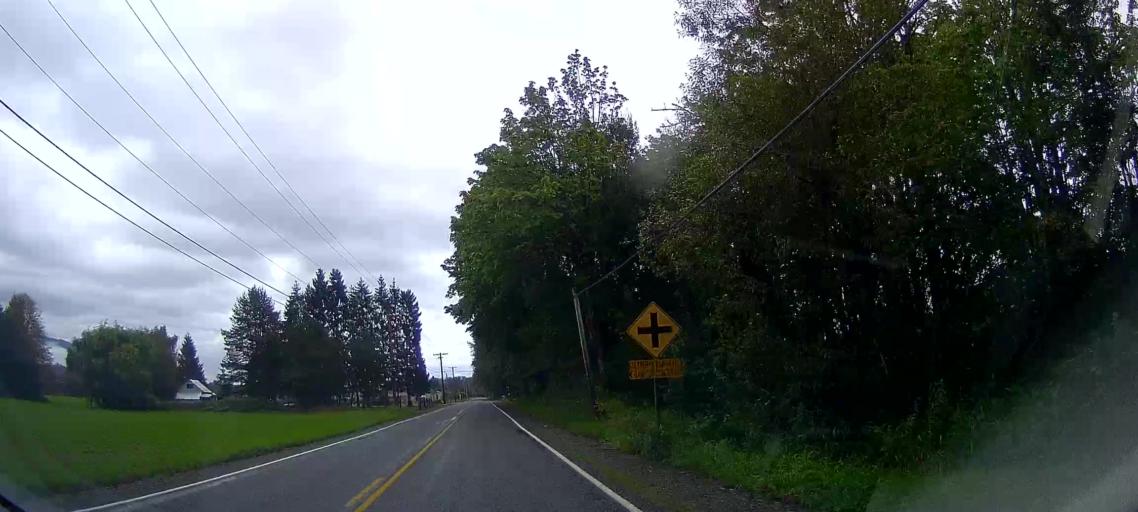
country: US
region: Washington
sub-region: Skagit County
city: Sedro-Woolley
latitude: 48.5272
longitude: -122.0407
